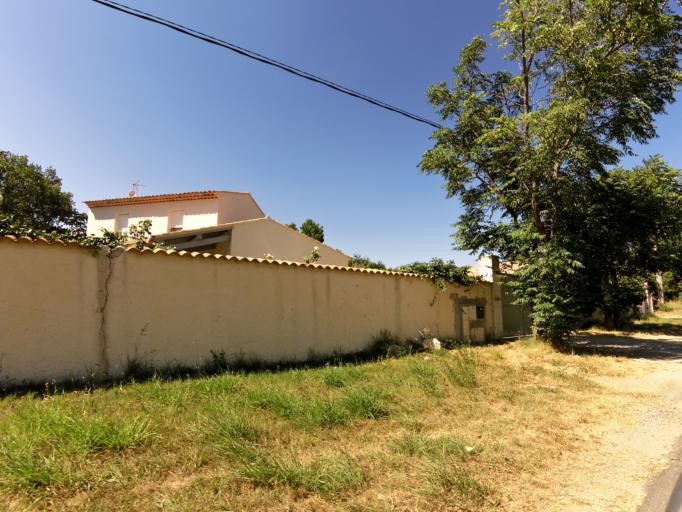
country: FR
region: Languedoc-Roussillon
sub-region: Departement de l'Herault
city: Boisseron
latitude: 43.7618
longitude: 4.0491
